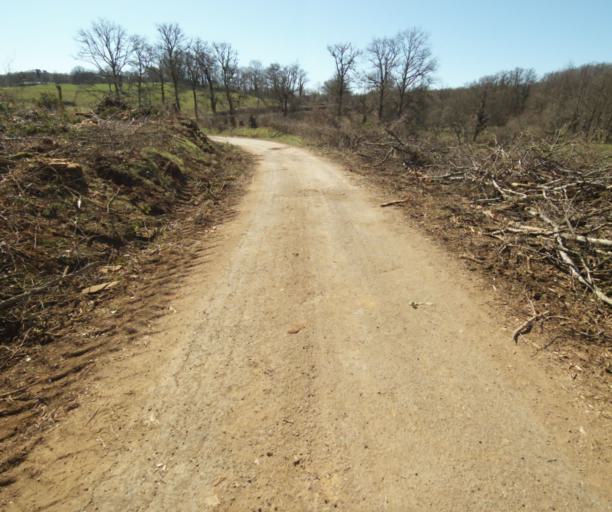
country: FR
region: Limousin
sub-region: Departement de la Correze
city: Chamboulive
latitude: 45.4094
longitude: 1.7429
